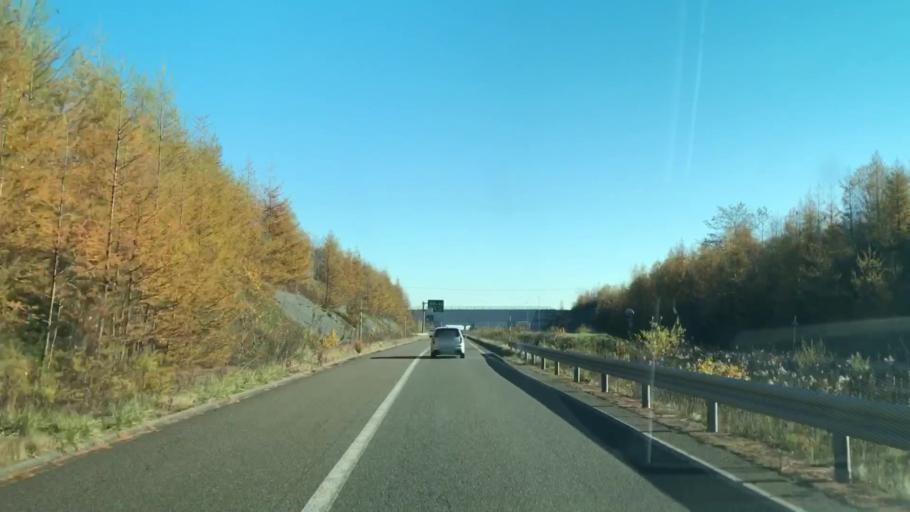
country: JP
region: Hokkaido
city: Otofuke
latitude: 42.9985
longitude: 142.8522
